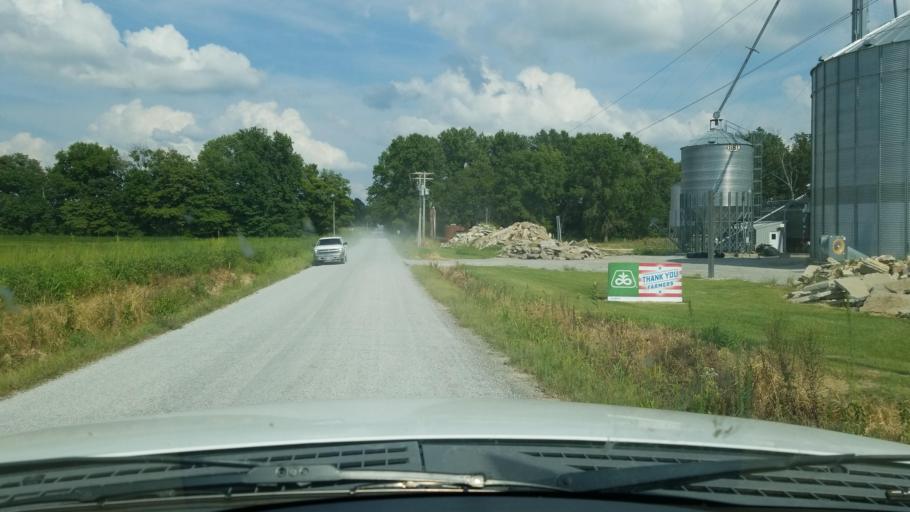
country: US
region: Illinois
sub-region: Saline County
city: Eldorado
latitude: 37.8344
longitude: -88.4432
